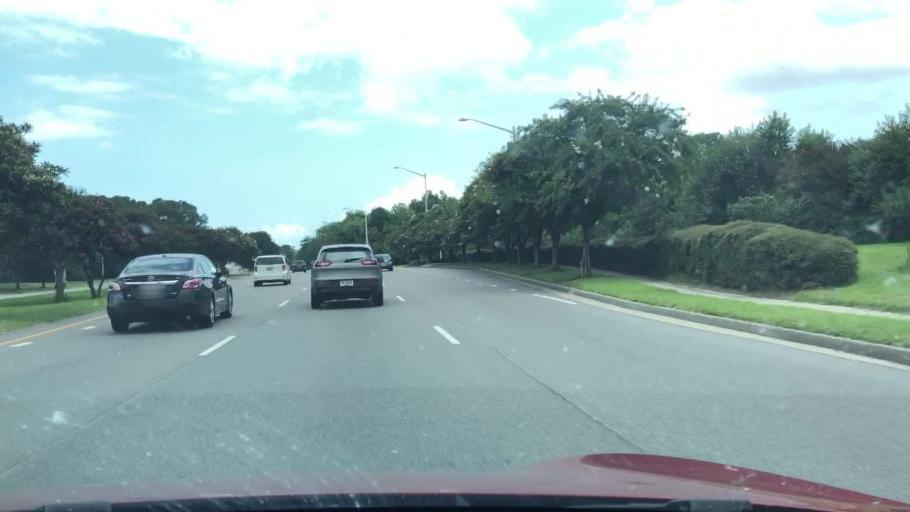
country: US
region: Virginia
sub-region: City of Chesapeake
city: Chesapeake
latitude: 36.8565
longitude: -76.1342
